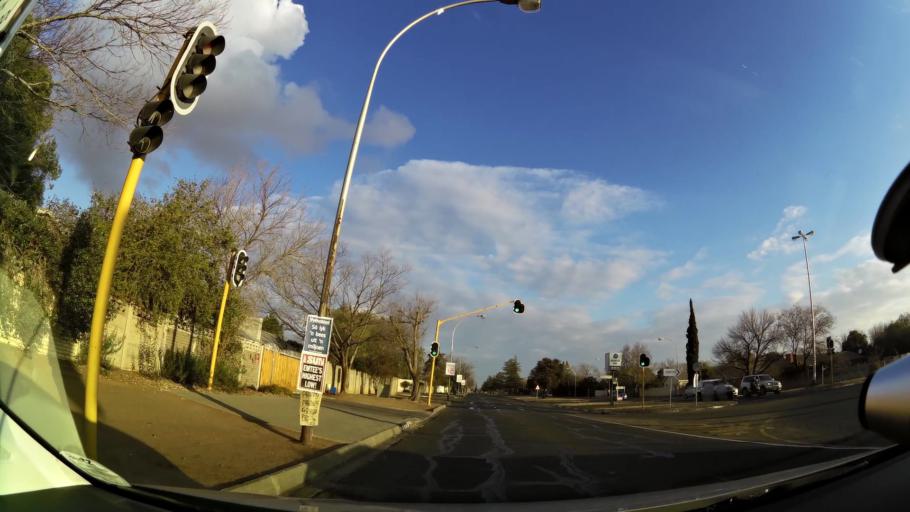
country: ZA
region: Orange Free State
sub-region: Mangaung Metropolitan Municipality
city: Bloemfontein
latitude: -29.1375
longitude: 26.1841
